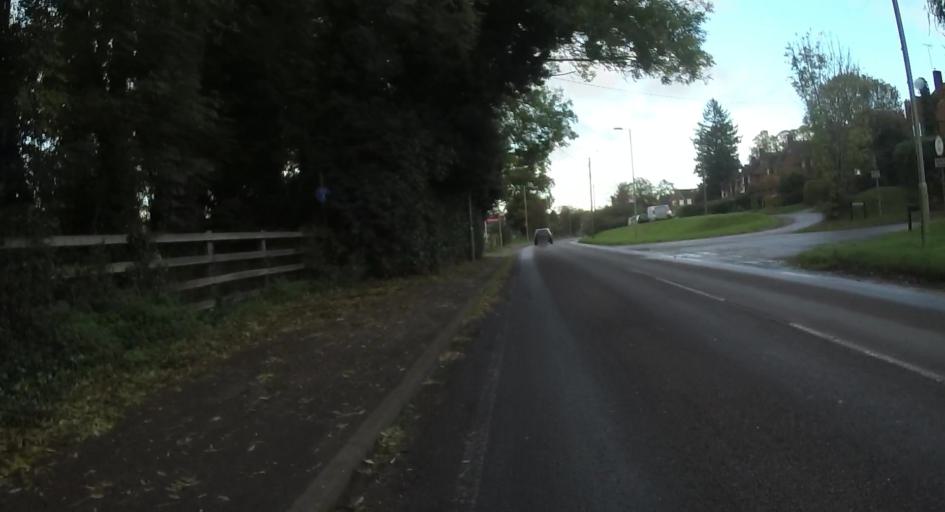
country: GB
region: England
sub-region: Hampshire
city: Alton
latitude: 51.1474
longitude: -0.9915
